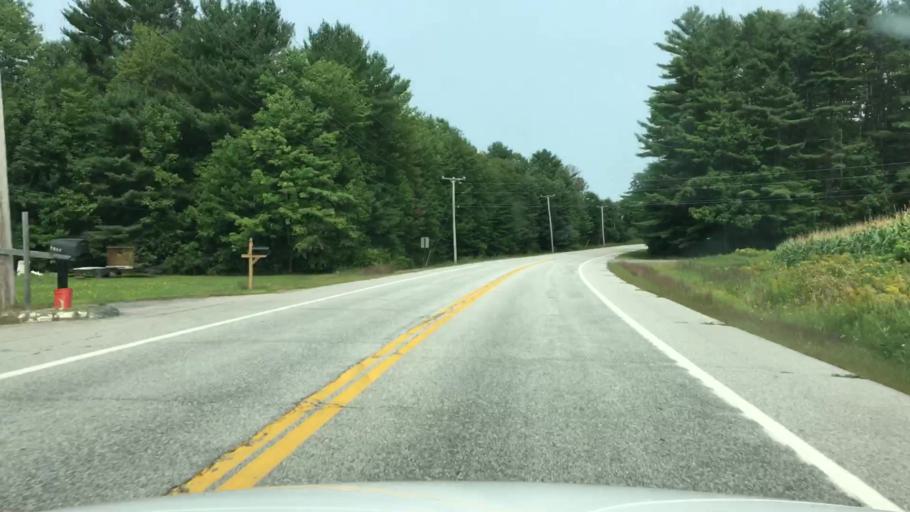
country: US
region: Maine
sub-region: Androscoggin County
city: Livermore Falls
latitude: 44.4128
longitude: -70.1434
